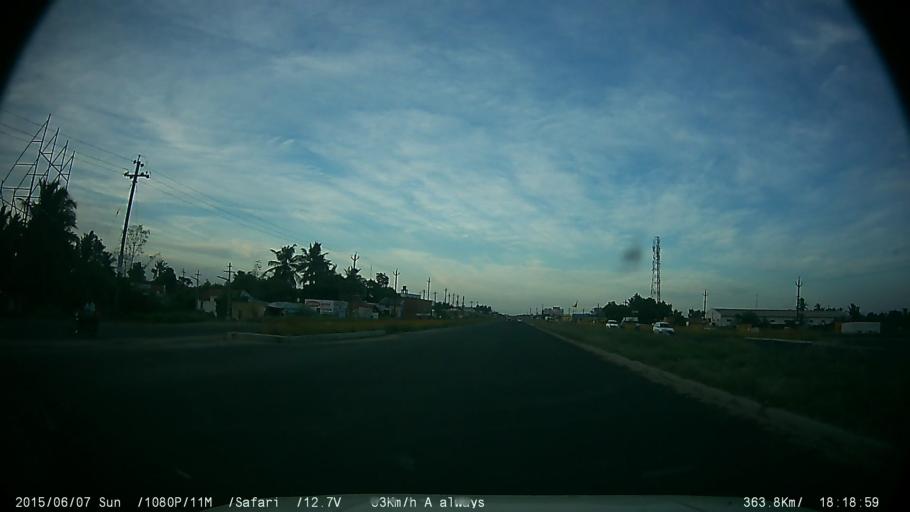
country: IN
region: Tamil Nadu
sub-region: Coimbatore
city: Sulur
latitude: 11.0756
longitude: 77.1106
